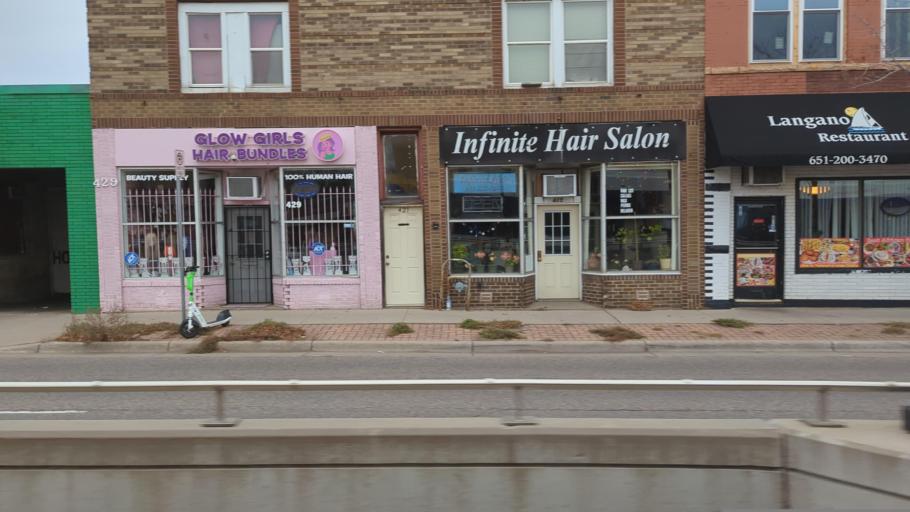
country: US
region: Minnesota
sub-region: Ramsey County
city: Saint Paul
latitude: 44.9559
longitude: -93.1179
